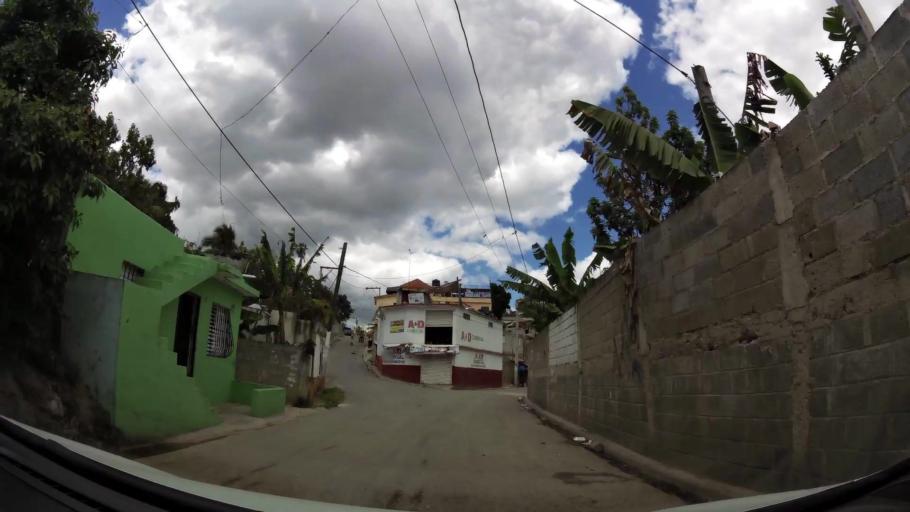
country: DO
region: Nacional
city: Ensanche Luperon
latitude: 18.5151
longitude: -69.9031
